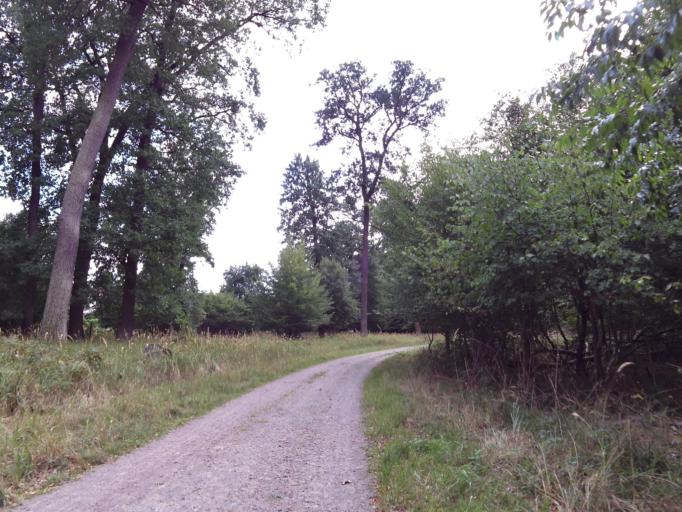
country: DE
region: Hesse
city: Morfelden-Walldorf
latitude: 49.9829
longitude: 8.5532
